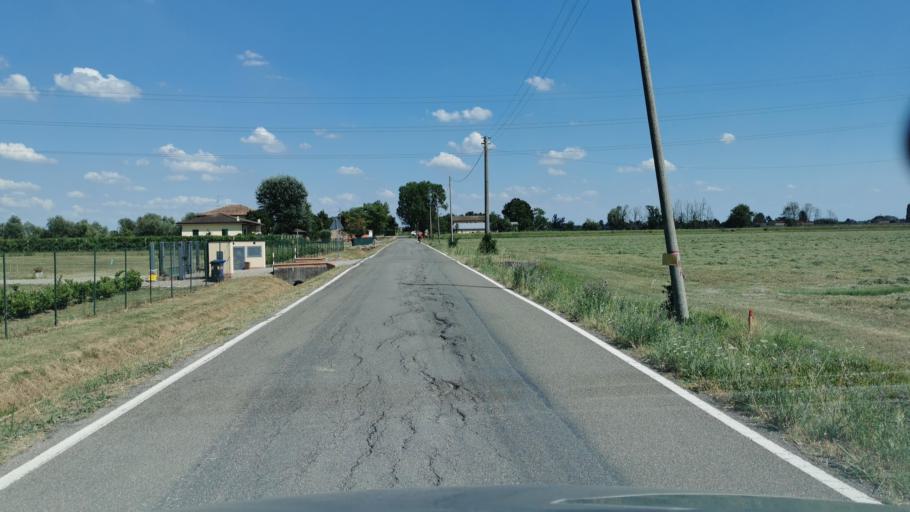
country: IT
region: Emilia-Romagna
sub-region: Provincia di Modena
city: Limidi
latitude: 44.7839
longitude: 10.9114
